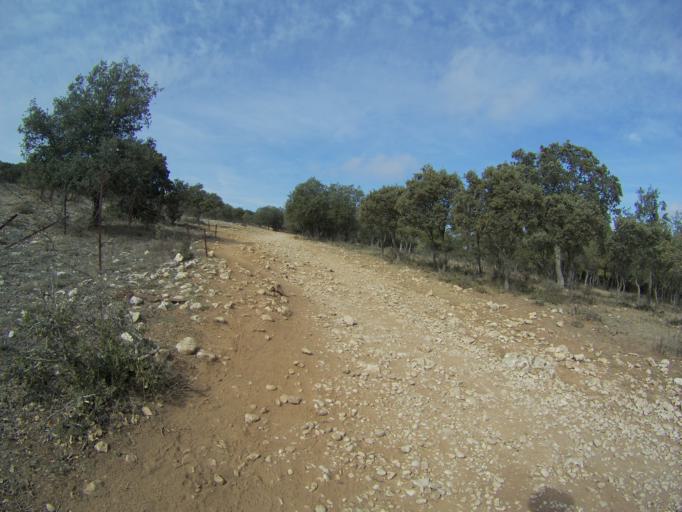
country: ES
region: Castille and Leon
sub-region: Provincia de Burgos
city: Atapuerca
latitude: 42.3792
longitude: -3.5242
